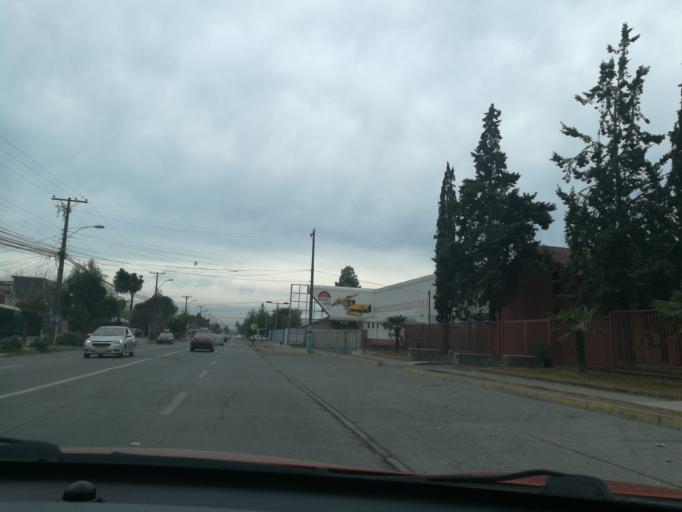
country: CL
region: O'Higgins
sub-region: Provincia de Cachapoal
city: Rancagua
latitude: -34.1544
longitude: -70.7376
